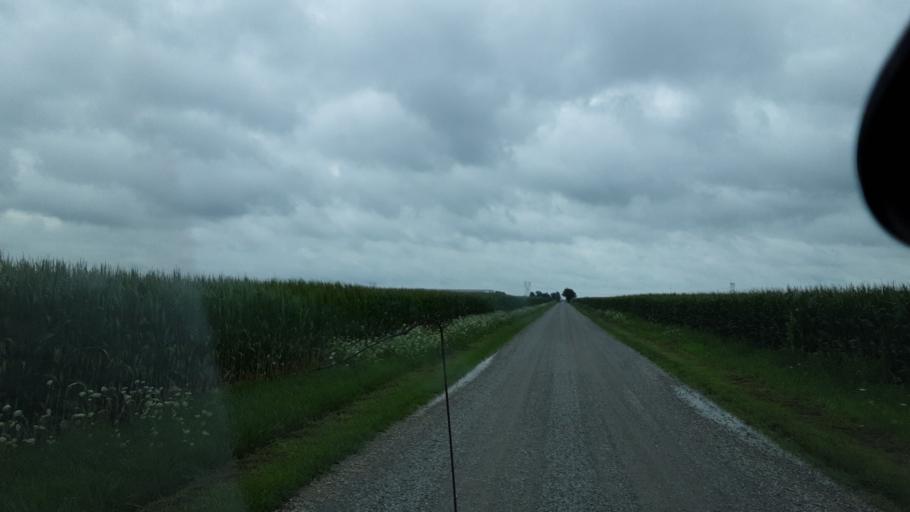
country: US
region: Indiana
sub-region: Wells County
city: Bluffton
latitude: 40.7689
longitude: -85.0711
